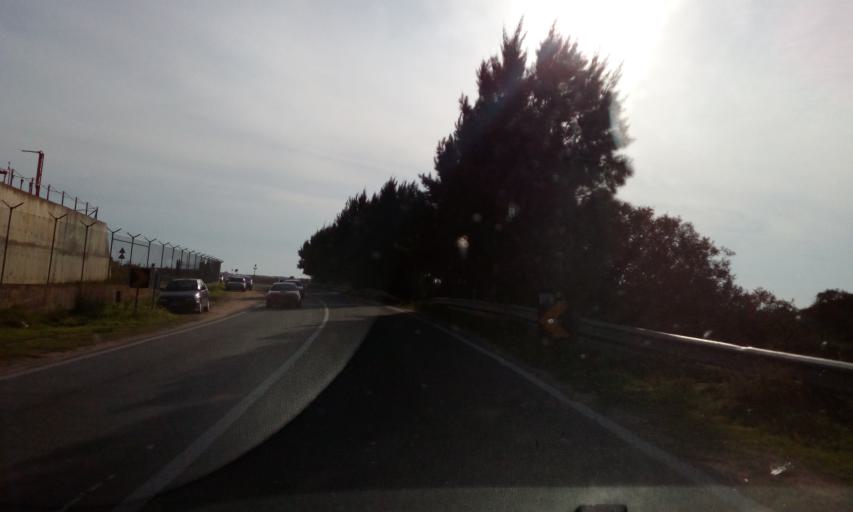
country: PT
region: Faro
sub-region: Faro
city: Faro
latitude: 37.0181
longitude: -7.9880
